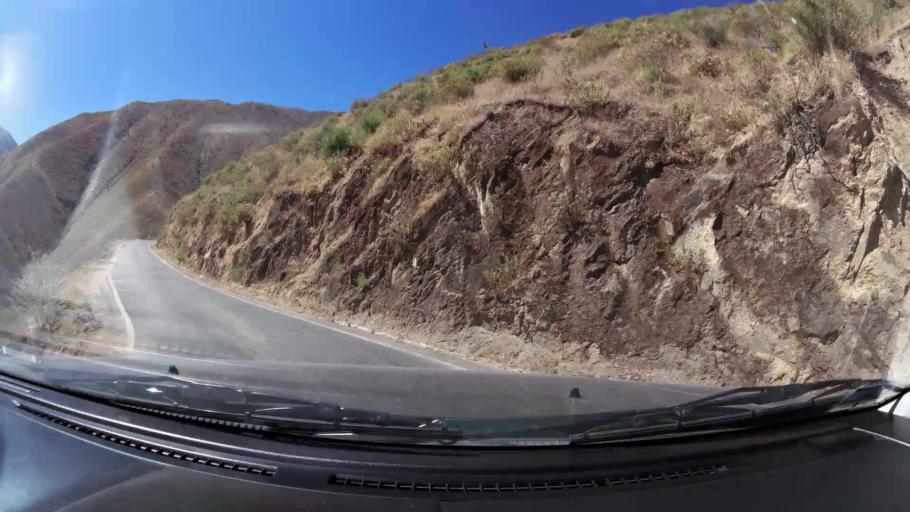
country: PE
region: Ica
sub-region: Provincia de Pisco
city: Huancano
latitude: -13.7227
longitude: -75.4569
